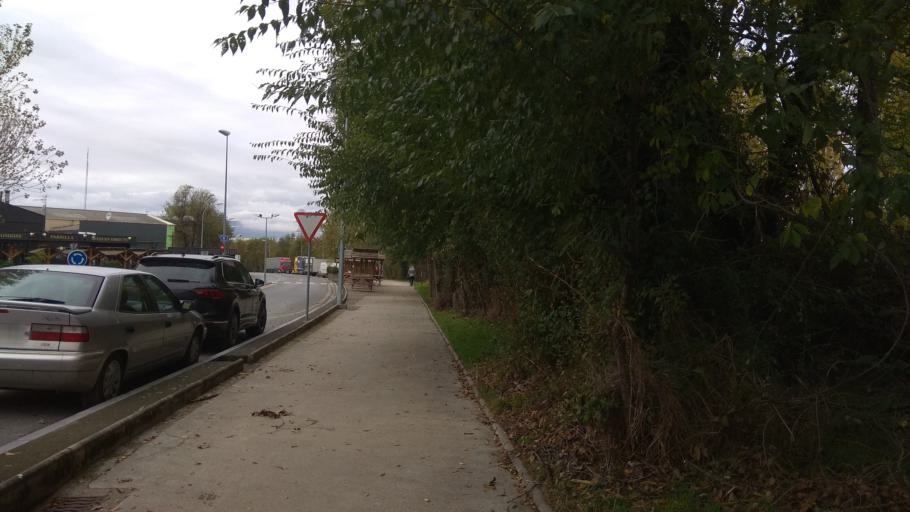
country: ES
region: Navarre
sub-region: Provincia de Navarra
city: Baranain
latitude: 42.8079
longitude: -1.6886
